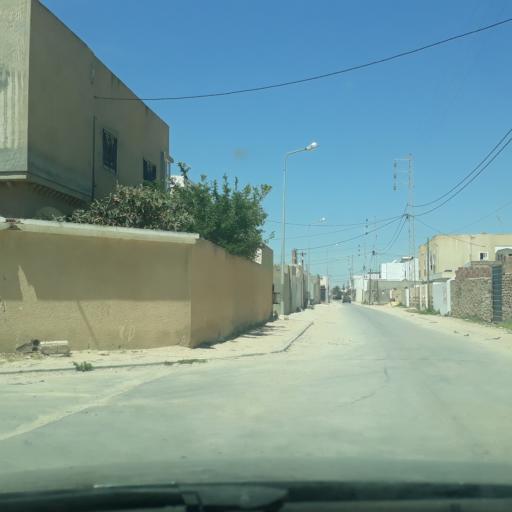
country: TN
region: Safaqis
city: Al Qarmadah
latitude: 34.8171
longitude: 10.7568
